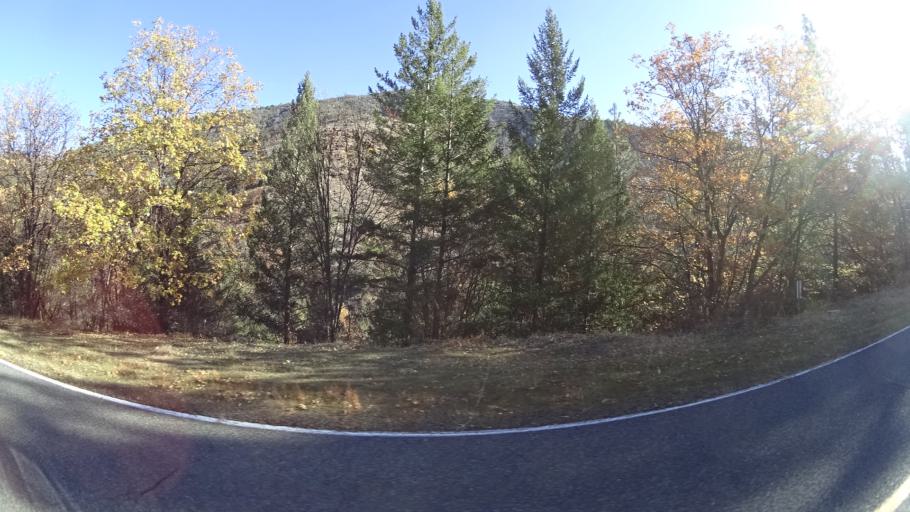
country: US
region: California
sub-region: Siskiyou County
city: Yreka
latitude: 41.9076
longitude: -122.8351
